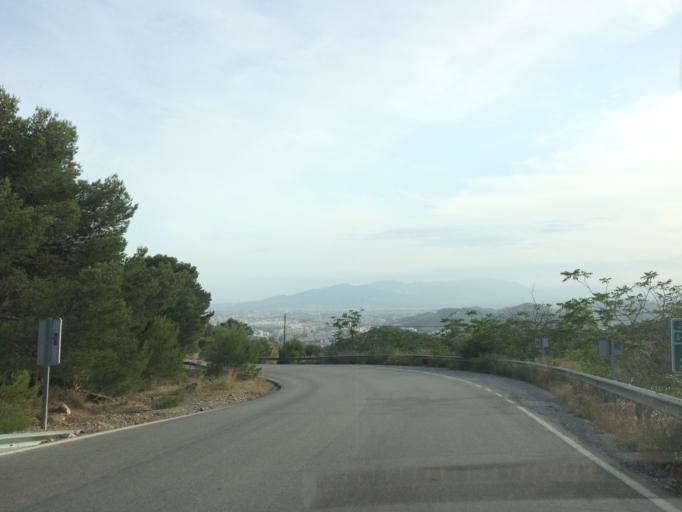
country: ES
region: Andalusia
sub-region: Provincia de Malaga
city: Malaga
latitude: 36.7582
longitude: -4.4078
